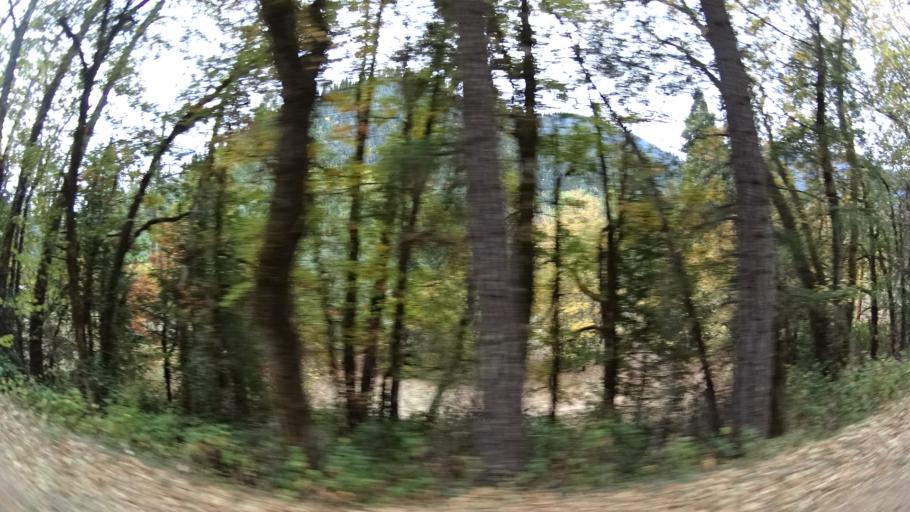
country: US
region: California
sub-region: Siskiyou County
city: Happy Camp
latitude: 41.8564
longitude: -123.3918
